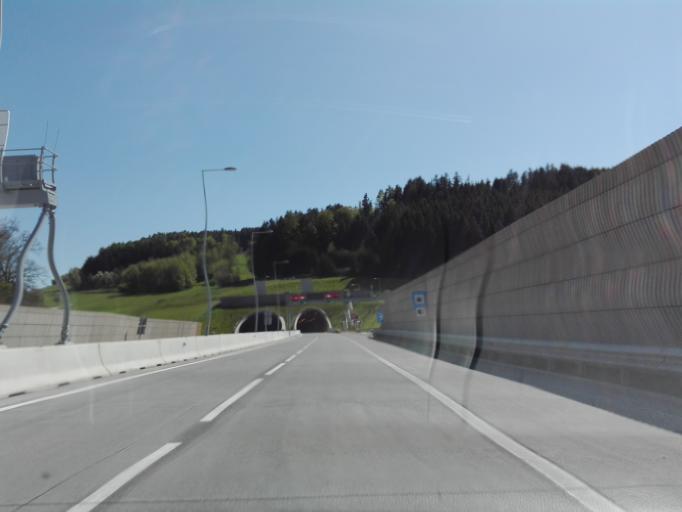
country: AT
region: Upper Austria
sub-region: Politischer Bezirk Urfahr-Umgebung
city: Alberndorf in der Riedmark
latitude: 48.4111
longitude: 14.4841
